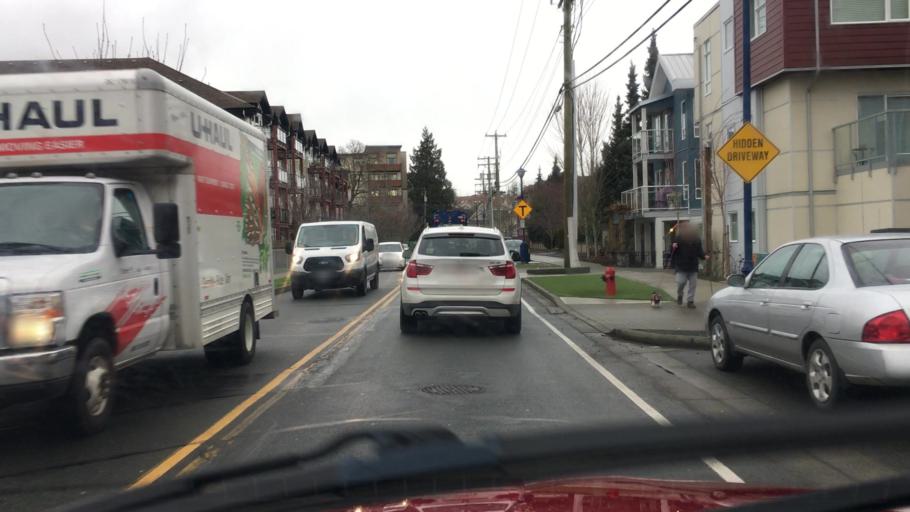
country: CA
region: British Columbia
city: Langford
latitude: 48.4524
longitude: -123.5044
